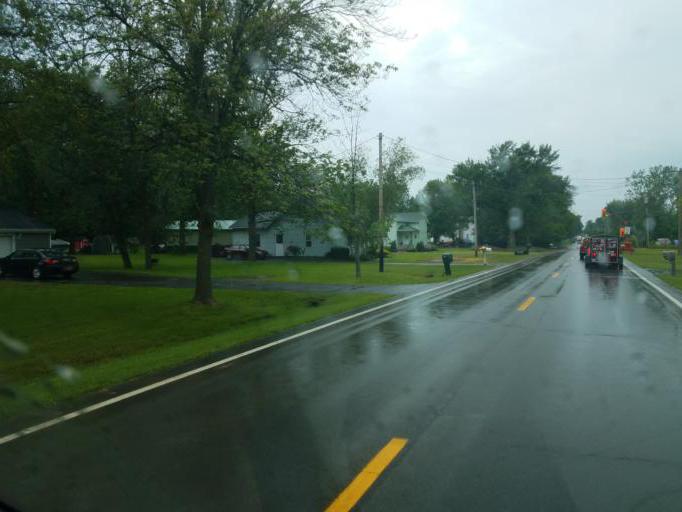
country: US
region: New York
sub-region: Niagara County
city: Ransomville
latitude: 43.2484
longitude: -78.9512
